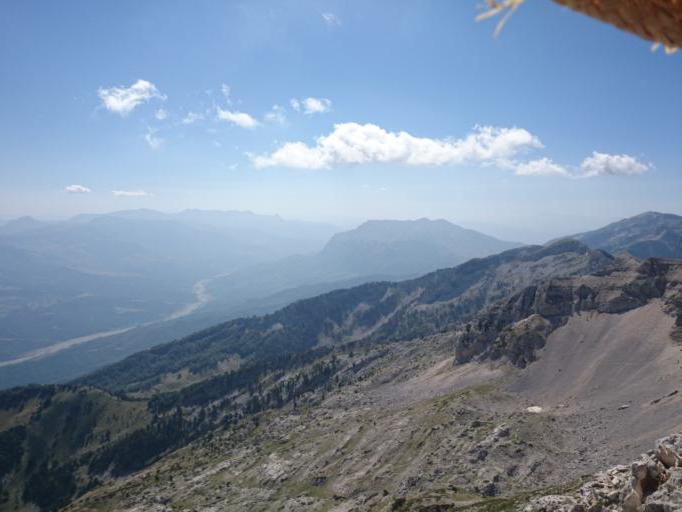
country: AL
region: Elbasan
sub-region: Rrethi i Gramshit
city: Kushove
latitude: 40.7055
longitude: 20.1436
